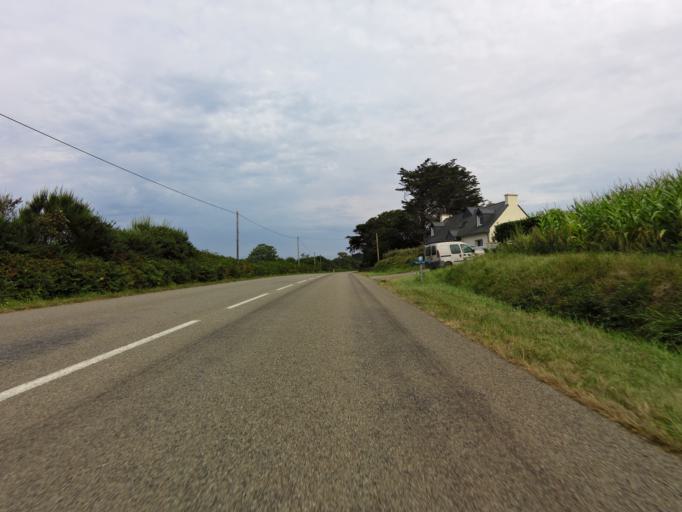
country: FR
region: Brittany
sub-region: Departement du Finistere
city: Poullan-sur-Mer
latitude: 48.0810
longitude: -4.4359
